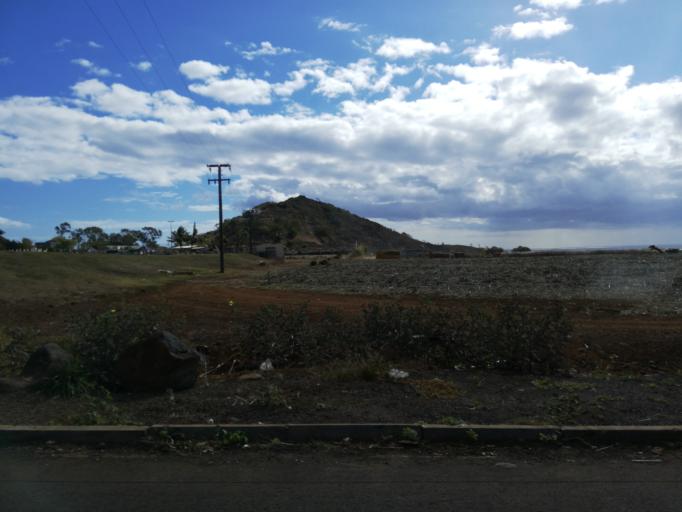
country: MU
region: Black River
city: Gros Cailloux
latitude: -20.2278
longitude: 57.4544
